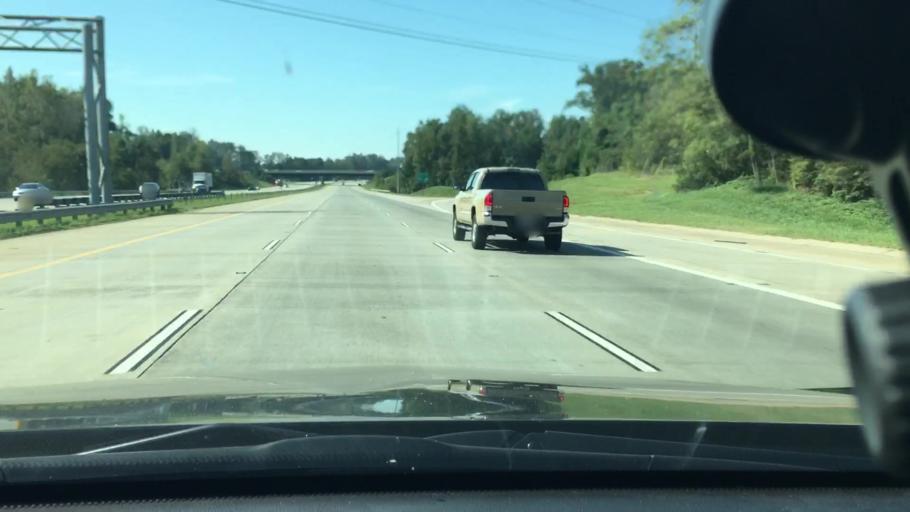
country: US
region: North Carolina
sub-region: Mecklenburg County
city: Huntersville
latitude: 35.3553
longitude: -80.8606
